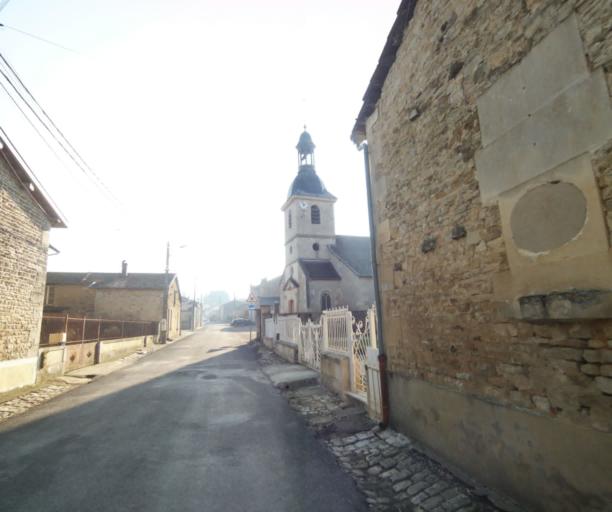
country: FR
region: Champagne-Ardenne
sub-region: Departement de la Haute-Marne
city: Chevillon
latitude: 48.4940
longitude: 5.0676
